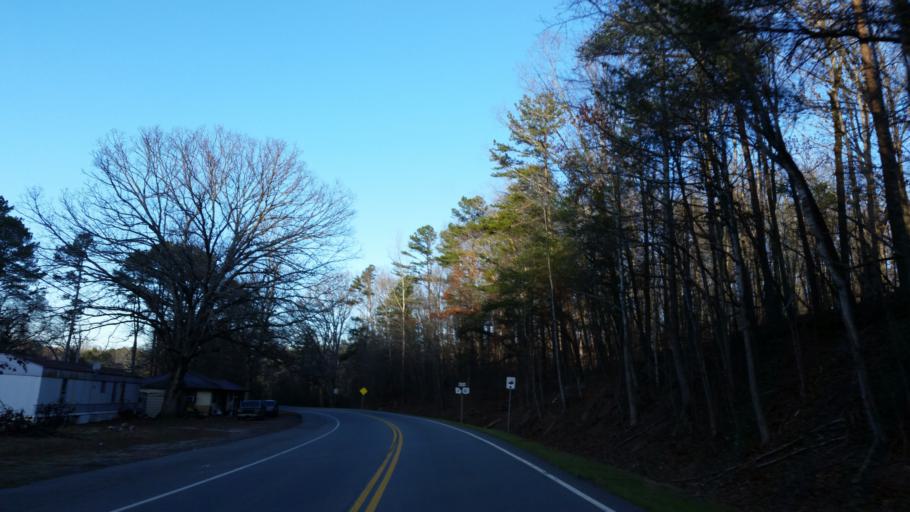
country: US
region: Georgia
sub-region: Gordon County
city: Calhoun
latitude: 34.6162
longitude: -84.9493
